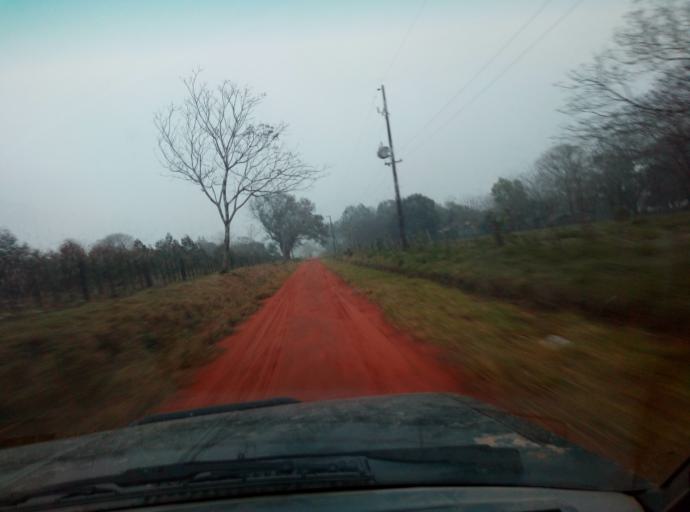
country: PY
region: Caaguazu
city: Doctor Cecilio Baez
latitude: -25.1563
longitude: -56.2799
